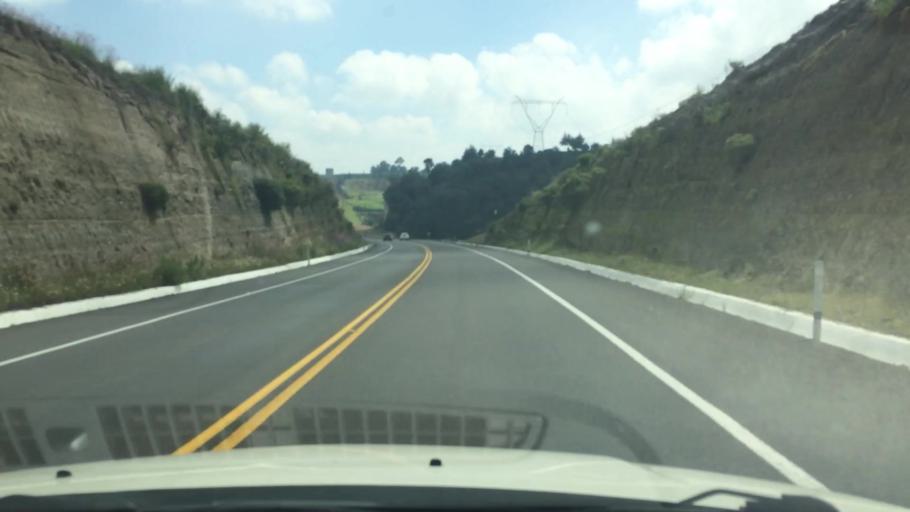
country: MX
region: Mexico
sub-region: Almoloya de Juarez
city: San Pedro de la Hortaliza (Ejido Almoloyan)
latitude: 19.3763
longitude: -99.8705
